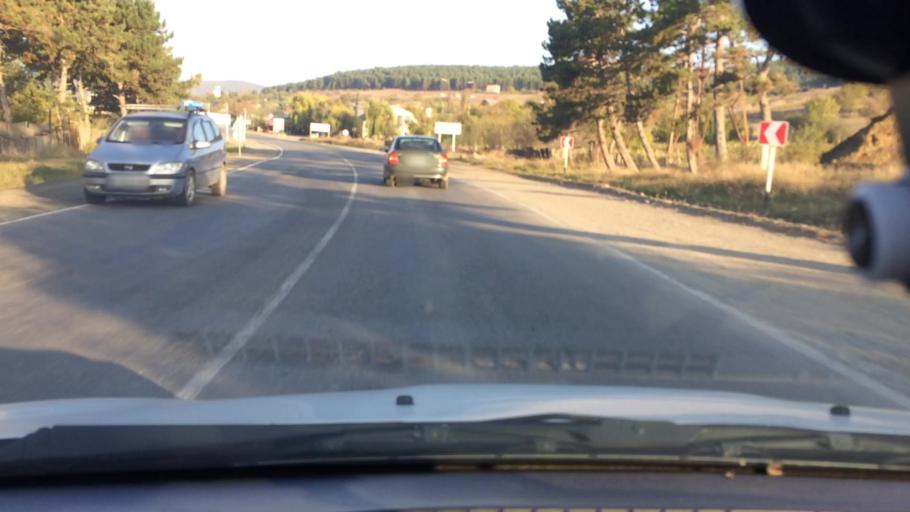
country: GE
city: Surami
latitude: 42.0121
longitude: 43.5776
